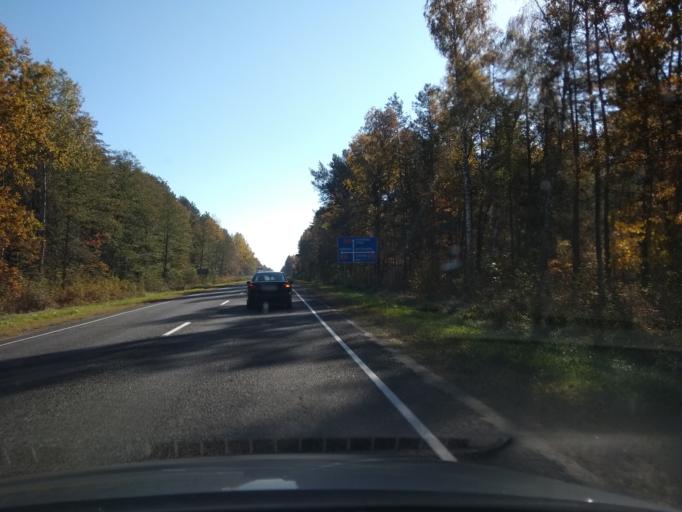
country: BY
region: Brest
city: Malaryta
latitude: 51.8948
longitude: 24.1345
